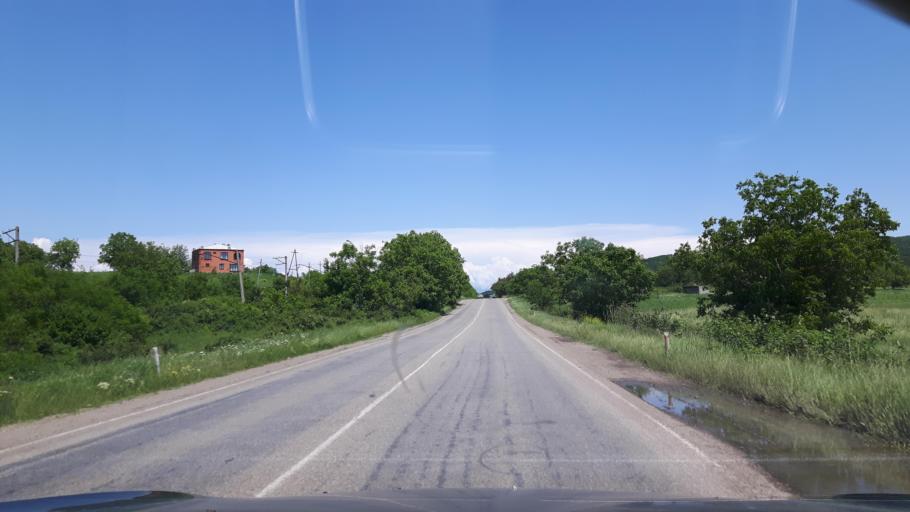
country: GE
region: Kakheti
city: Sighnaghi
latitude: 41.6295
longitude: 45.8137
